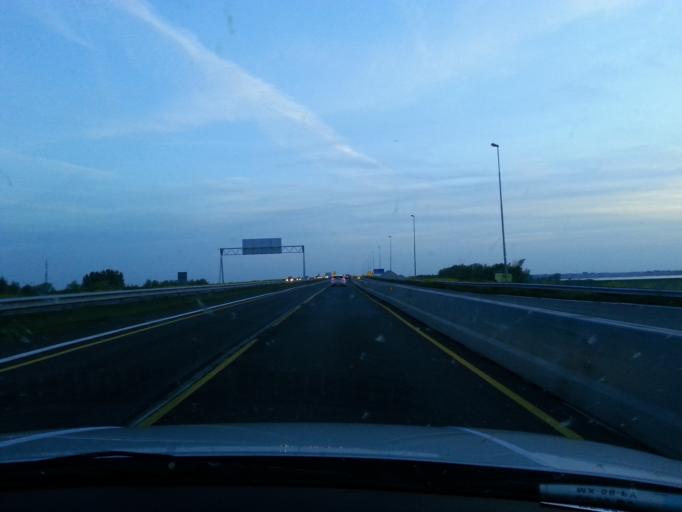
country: NL
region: Utrecht
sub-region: Gemeente Bunschoten
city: Spakenburg
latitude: 52.3088
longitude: 5.3237
